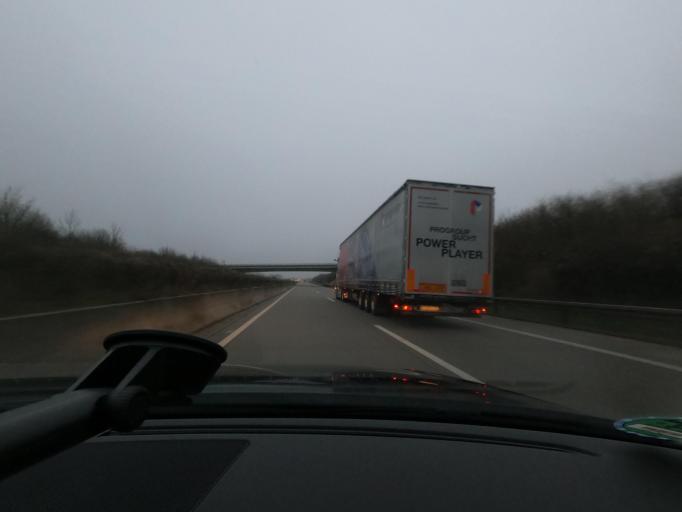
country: DE
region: Thuringia
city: Zimmernsupra
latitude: 50.9723
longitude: 10.9188
